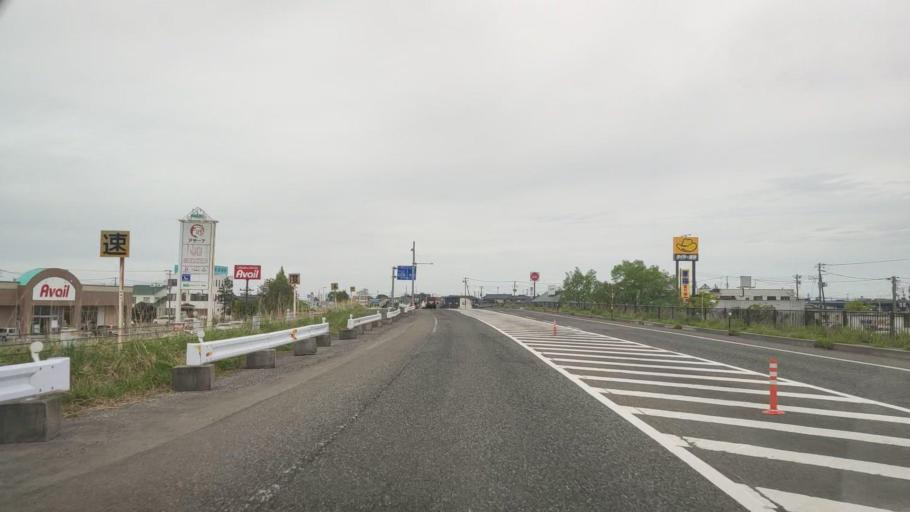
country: JP
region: Niigata
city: Niitsu-honcho
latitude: 37.7921
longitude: 139.1108
